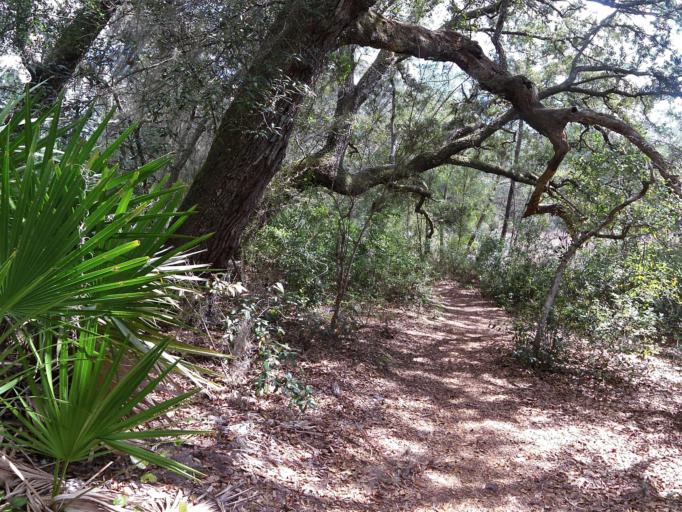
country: US
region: Florida
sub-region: Clay County
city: Keystone Heights
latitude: 29.7872
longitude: -81.8763
